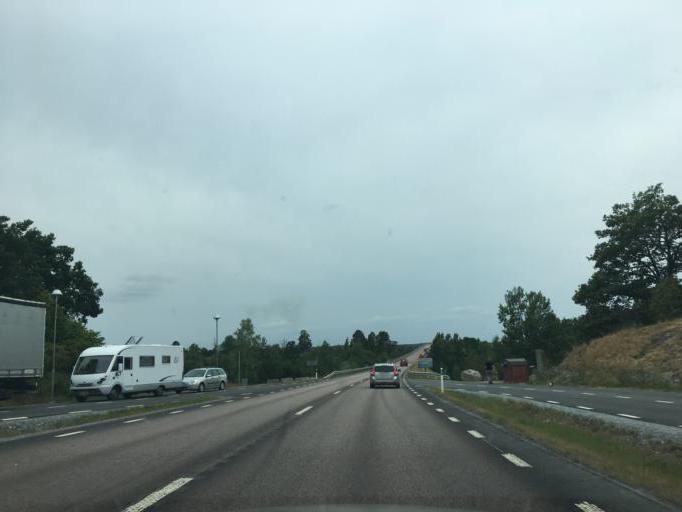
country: SE
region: Soedermanland
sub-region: Strangnas Kommun
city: Strangnas
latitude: 59.4016
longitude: 17.0177
